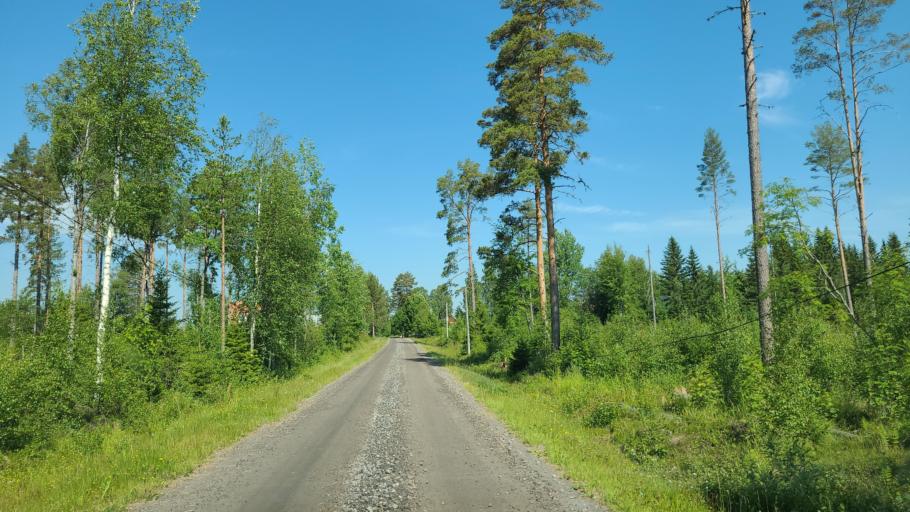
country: SE
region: Vaesterbotten
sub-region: Robertsfors Kommun
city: Robertsfors
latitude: 64.0901
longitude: 20.8491
